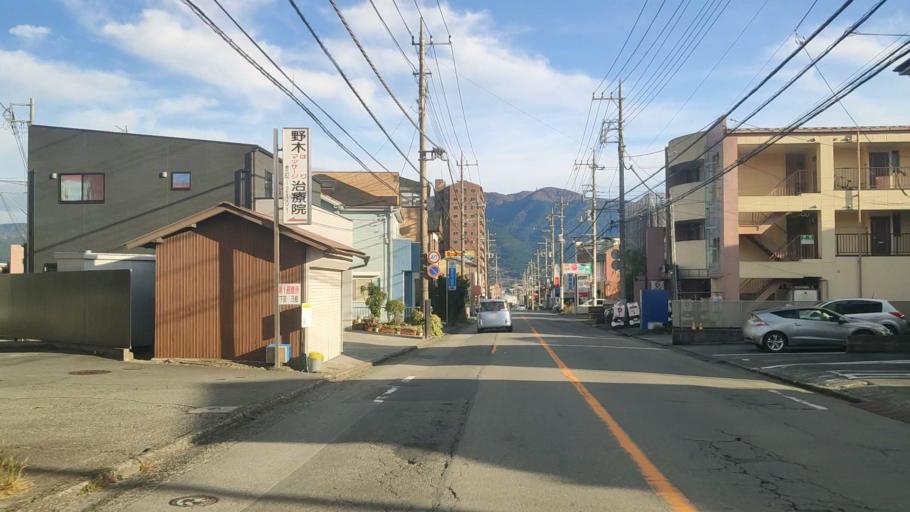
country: JP
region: Shizuoka
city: Gotemba
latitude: 35.3031
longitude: 138.9279
